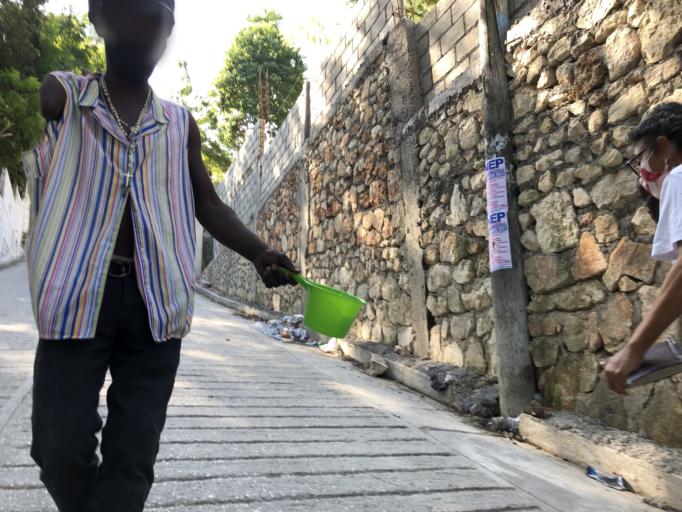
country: HT
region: Ouest
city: Port-au-Prince
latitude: 18.5239
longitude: -72.3219
